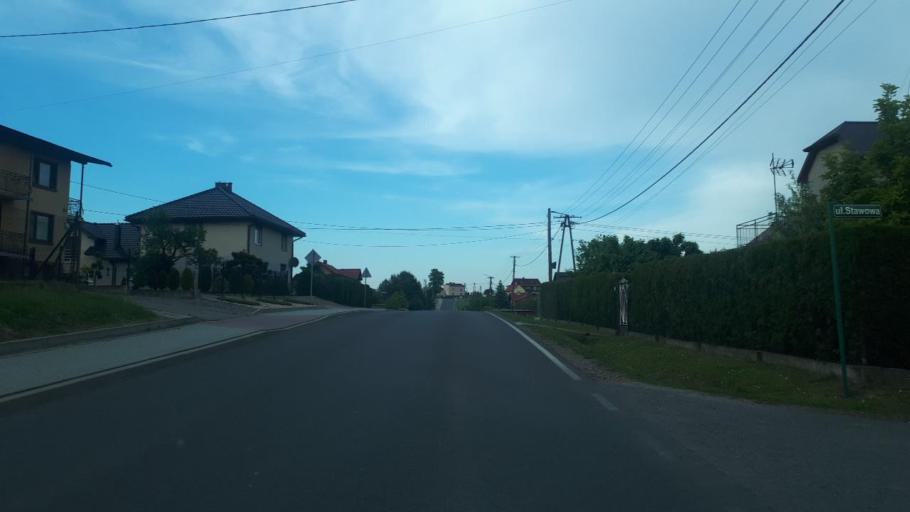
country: PL
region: Silesian Voivodeship
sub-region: Powiat bielski
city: Pisarzowice
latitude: 49.9039
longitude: 19.1283
